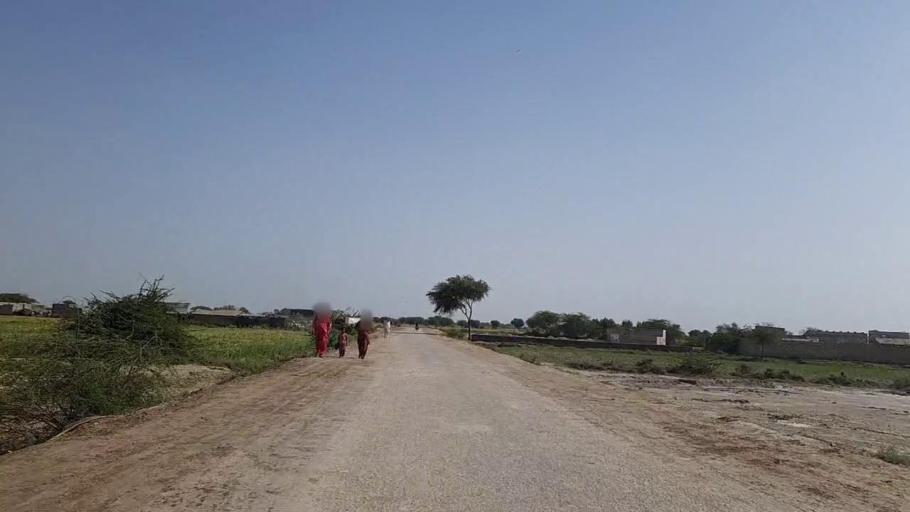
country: PK
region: Sindh
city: Jati
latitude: 24.3553
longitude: 68.2744
